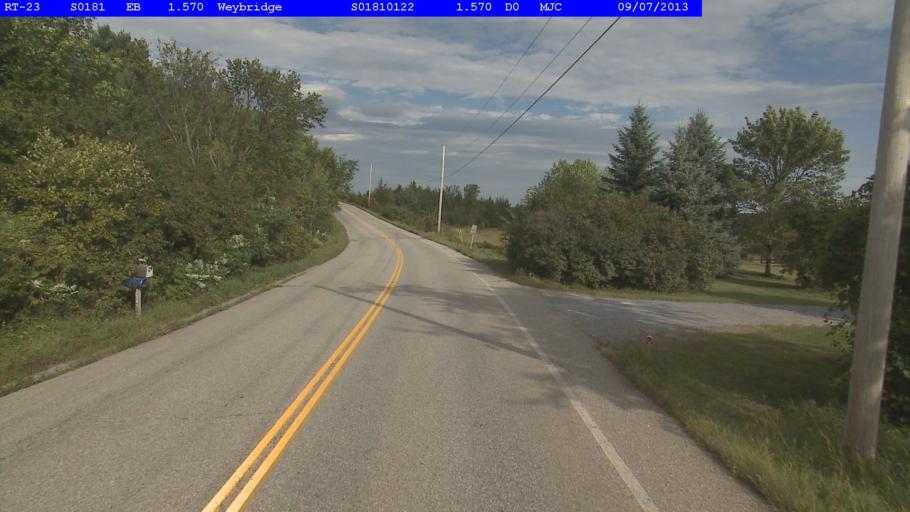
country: US
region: Vermont
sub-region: Addison County
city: Middlebury (village)
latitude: 44.0343
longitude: -73.2050
